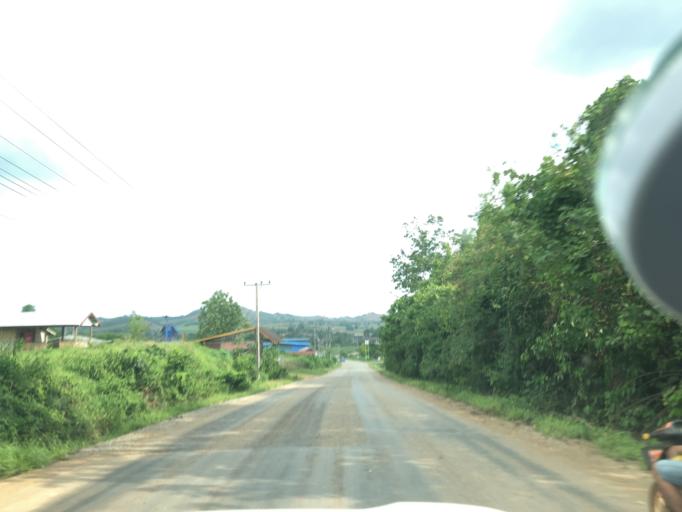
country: TH
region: Uttaradit
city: Ban Khok
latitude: 18.1202
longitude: 101.3728
